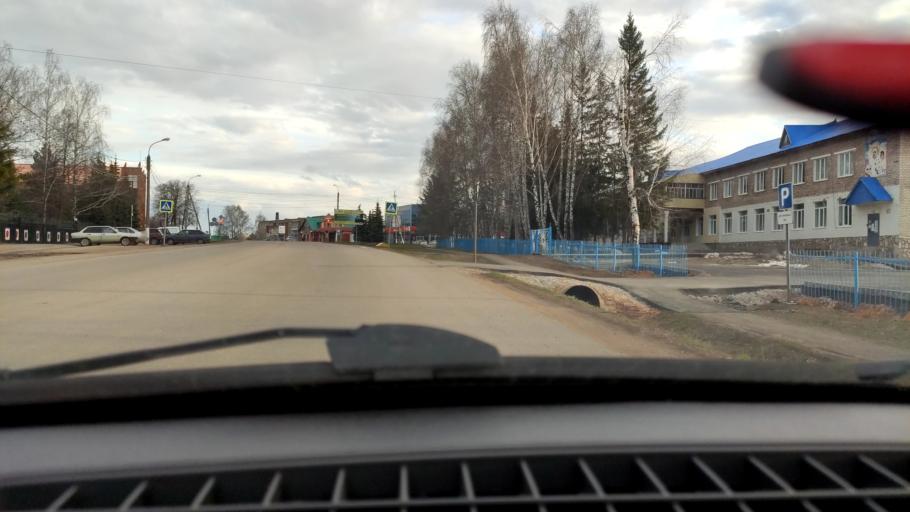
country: RU
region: Bashkortostan
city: Tolbazy
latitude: 54.0122
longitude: 55.8864
